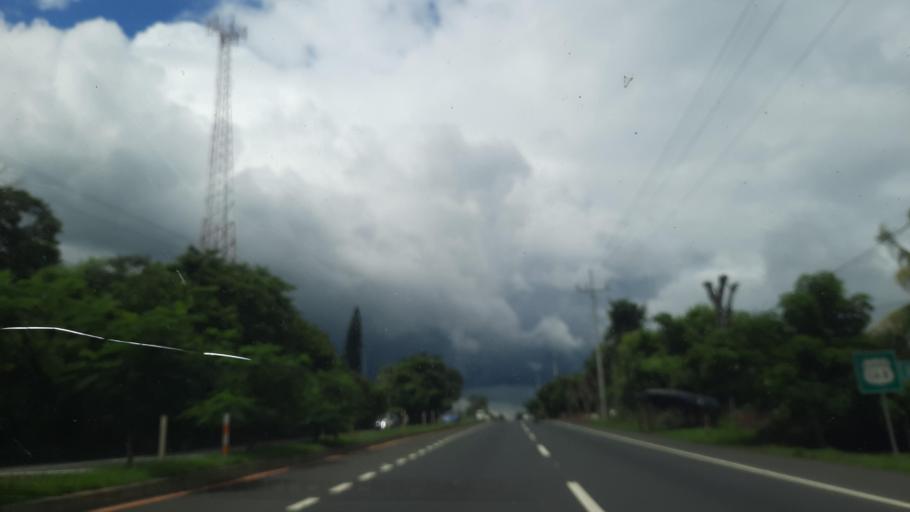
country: SV
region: Sonsonate
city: Izalco
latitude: 13.7529
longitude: -89.5859
